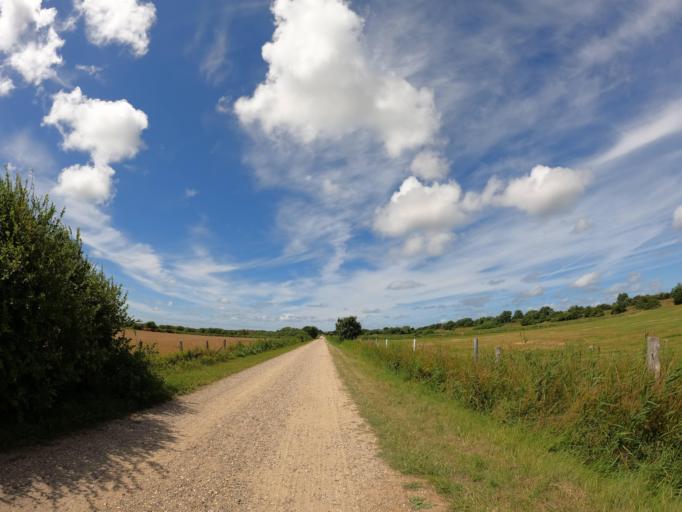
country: DE
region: Schleswig-Holstein
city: Keitum
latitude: 54.8928
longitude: 8.3541
